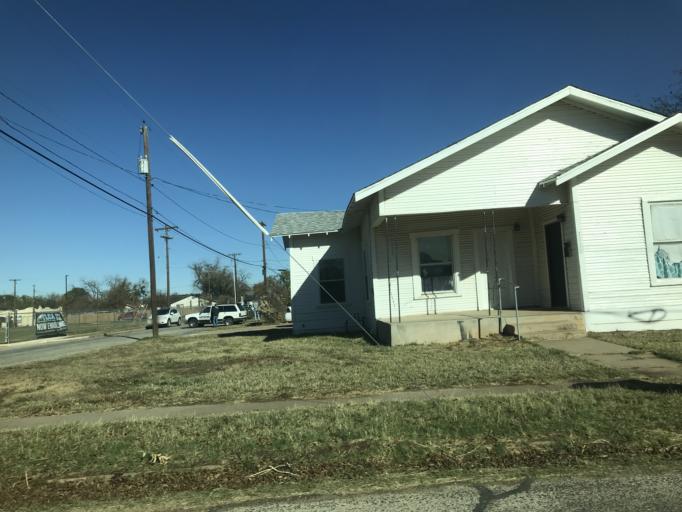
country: US
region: Texas
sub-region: Taylor County
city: Abilene
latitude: 32.4579
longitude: -99.7425
